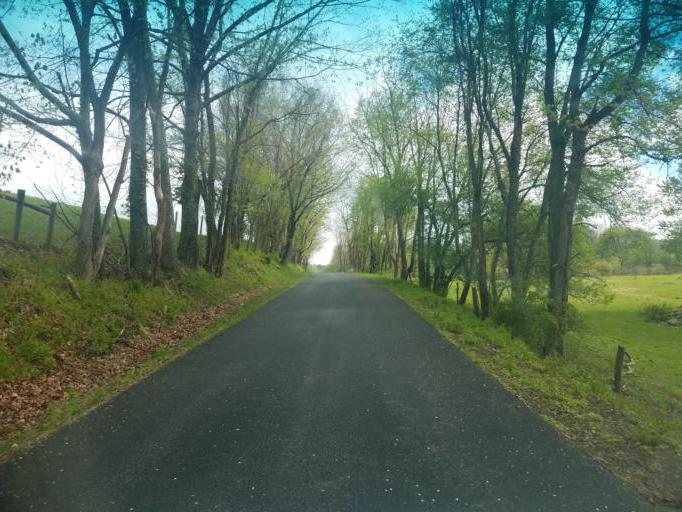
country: US
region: Virginia
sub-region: Smyth County
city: Atkins
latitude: 36.9479
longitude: -81.4134
